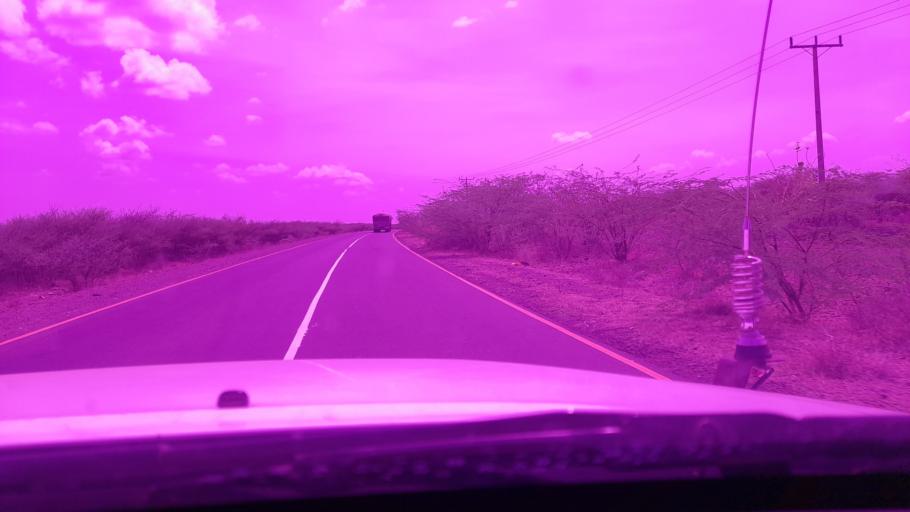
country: ET
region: Afar
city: Awash
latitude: 9.3488
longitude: 40.2959
